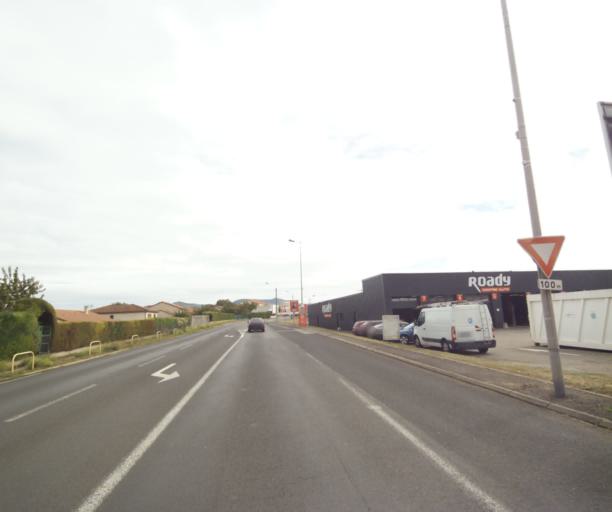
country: FR
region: Auvergne
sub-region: Departement du Puy-de-Dome
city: Le Cendre
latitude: 45.7287
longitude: 3.1870
